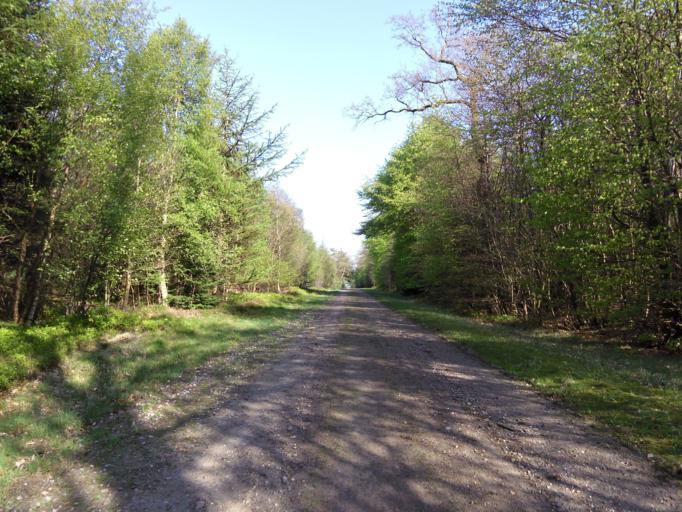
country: DK
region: South Denmark
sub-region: Tonder Kommune
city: Toftlund
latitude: 55.1933
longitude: 8.9545
